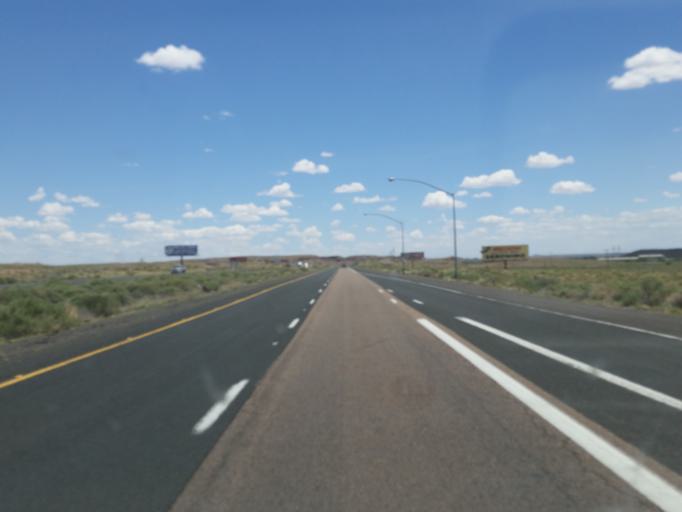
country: US
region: Arizona
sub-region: Navajo County
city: Joseph City
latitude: 34.9504
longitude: -110.3057
